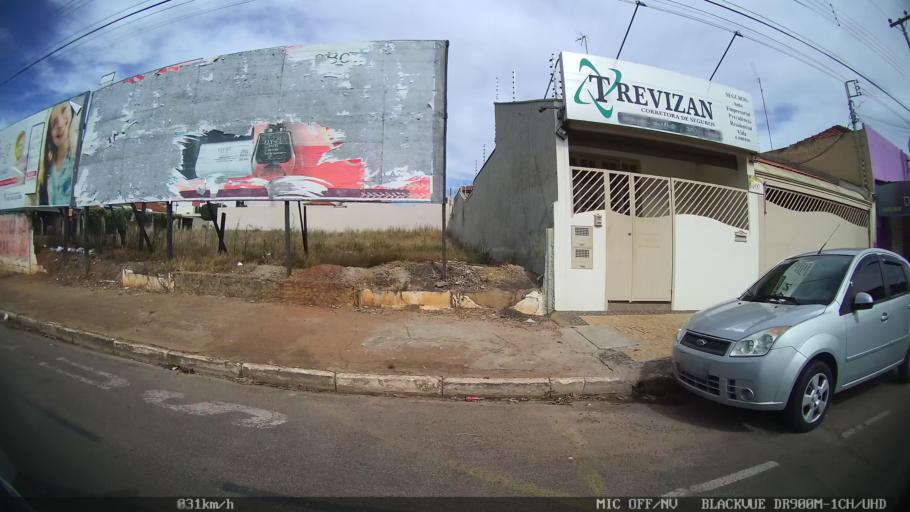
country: BR
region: Sao Paulo
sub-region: Catanduva
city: Catanduva
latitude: -21.1410
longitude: -48.9634
